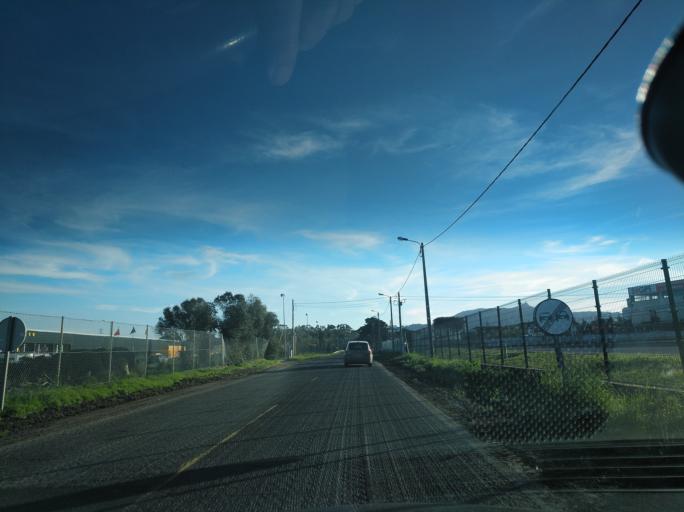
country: PT
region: Lisbon
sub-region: Sintra
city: Sintra
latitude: 38.8242
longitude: -9.3681
